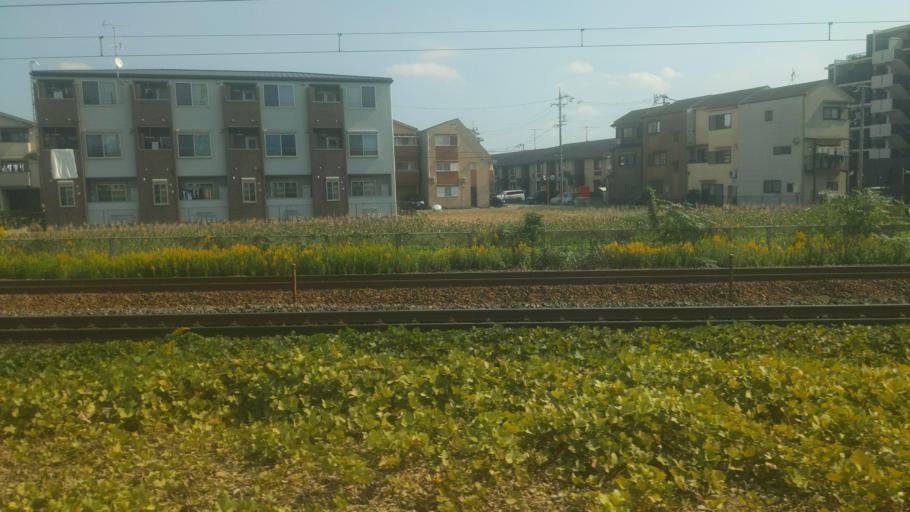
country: JP
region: Kyoto
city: Muko
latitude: 34.9669
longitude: 135.7113
